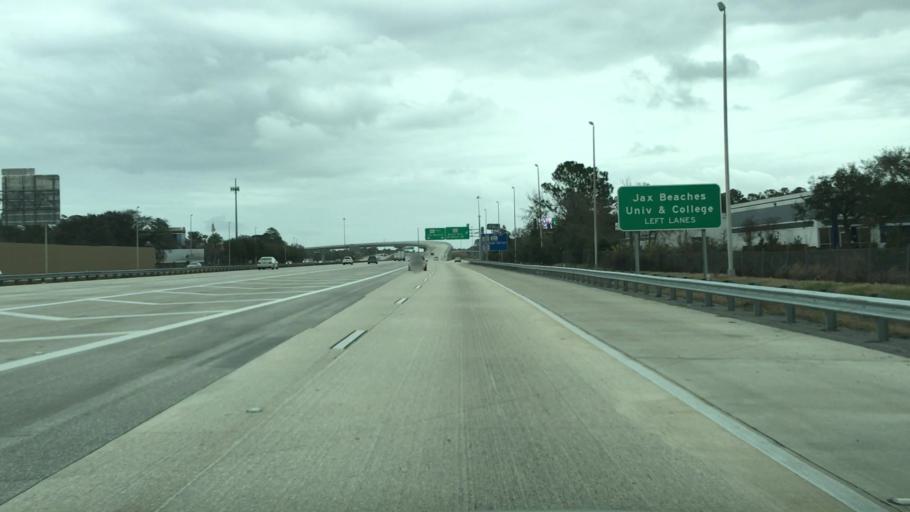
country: US
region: Florida
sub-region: Duval County
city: Jacksonville
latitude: 30.2544
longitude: -81.6000
